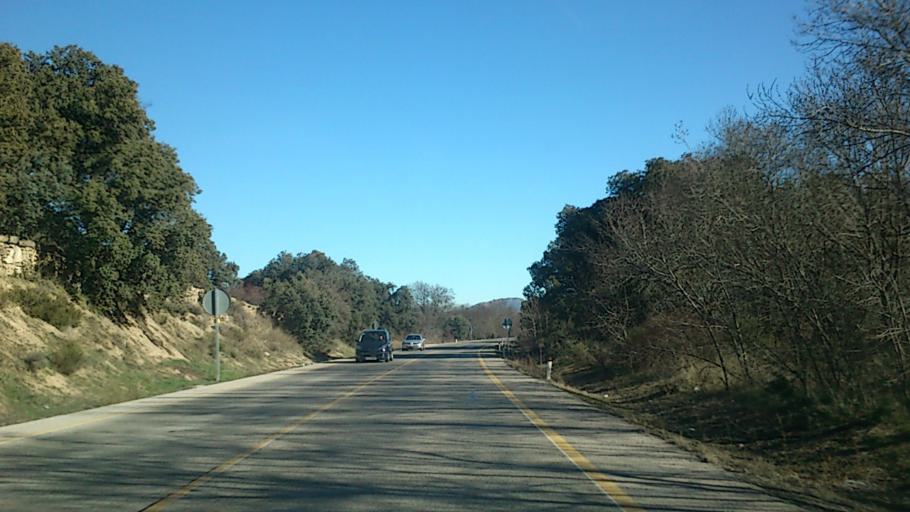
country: ES
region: Madrid
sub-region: Provincia de Madrid
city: Guadarrama
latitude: 40.6526
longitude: -4.0641
